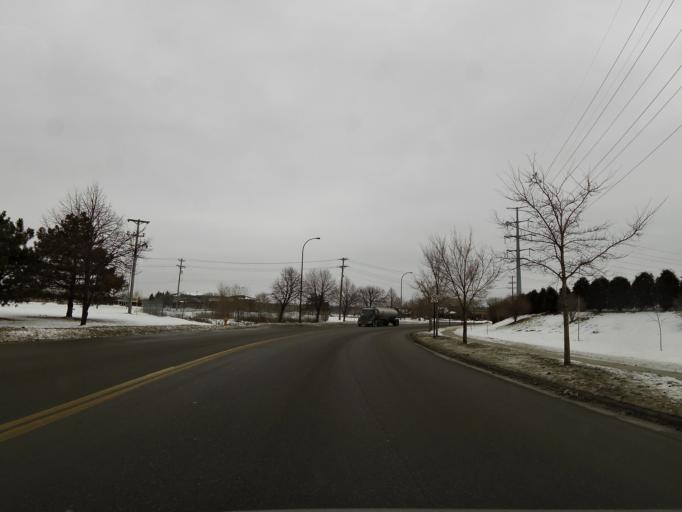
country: US
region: Minnesota
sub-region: Dakota County
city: South Saint Paul
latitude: 44.8854
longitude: -93.0244
